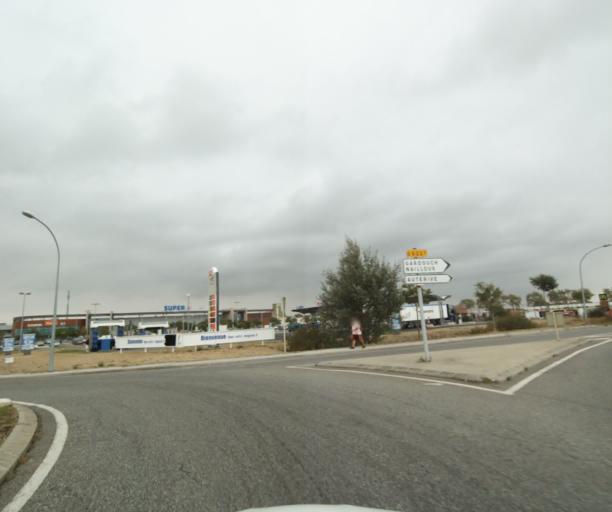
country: FR
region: Midi-Pyrenees
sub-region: Departement de la Haute-Garonne
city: Villefranche-de-Lauragais
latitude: 43.3995
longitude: 1.7023
